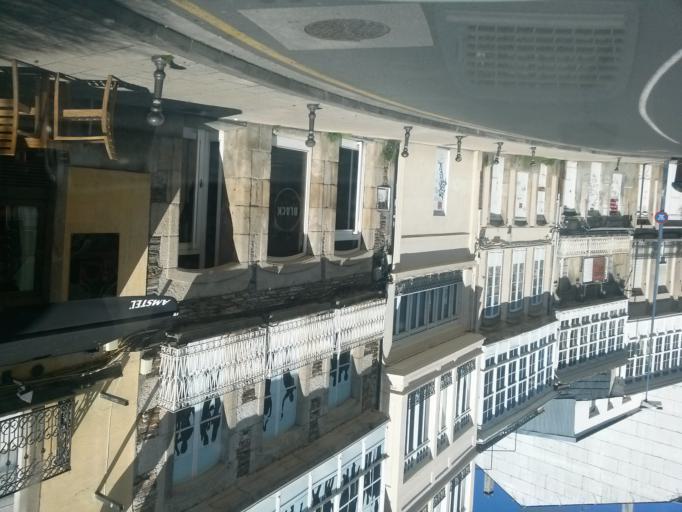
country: ES
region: Galicia
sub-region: Provincia de Lugo
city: Lugo
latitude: 43.0131
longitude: -7.5544
